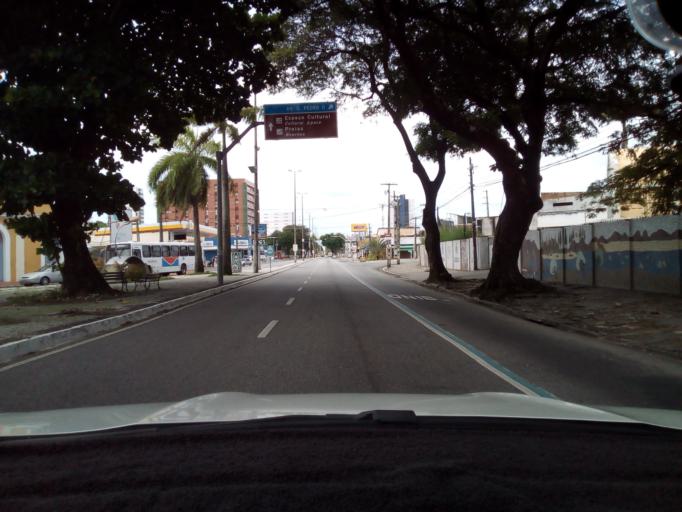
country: BR
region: Paraiba
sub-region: Joao Pessoa
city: Joao Pessoa
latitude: -7.1199
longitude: -34.8685
